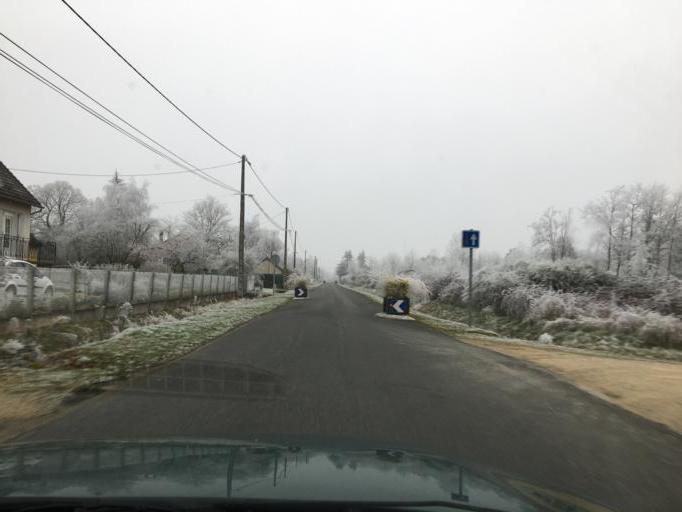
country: FR
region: Centre
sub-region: Departement du Loir-et-Cher
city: Chaumont-sur-Tharonne
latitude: 47.6308
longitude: 1.8482
